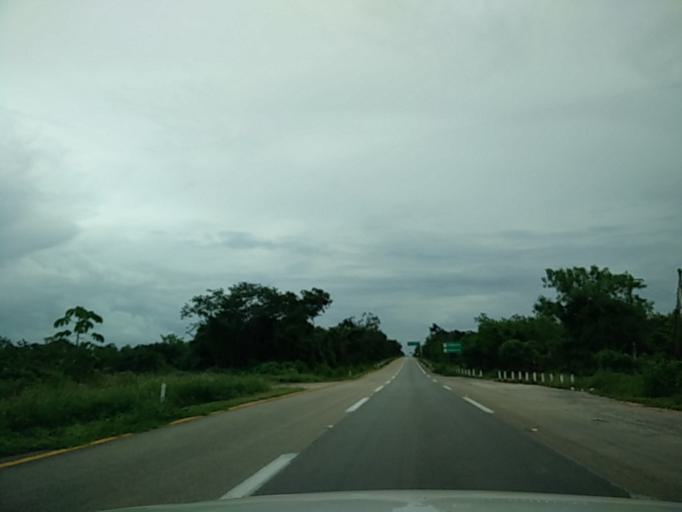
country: MX
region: Quintana Roo
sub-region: Lazaro Cardenas
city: Nuevo Xcan
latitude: 20.8771
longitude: -87.6312
